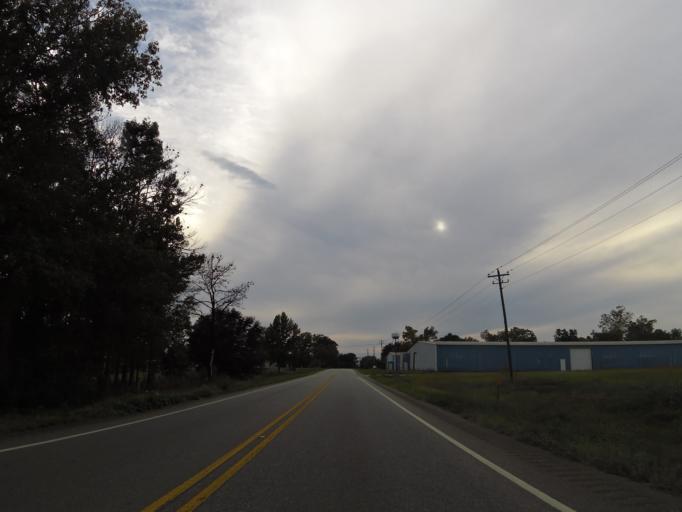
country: US
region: Alabama
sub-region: Monroe County
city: Frisco City
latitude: 31.3083
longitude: -87.4928
